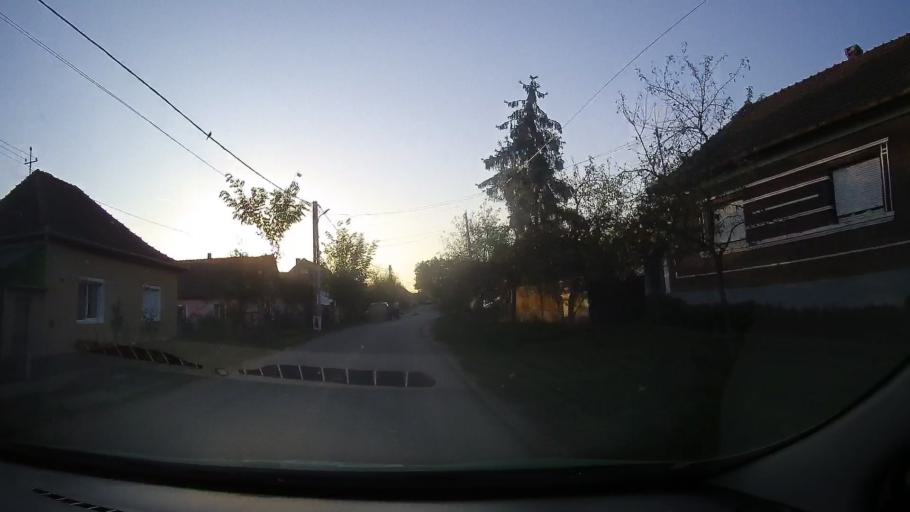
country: RO
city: Dioszeg
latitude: 47.2498
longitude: 22.0031
